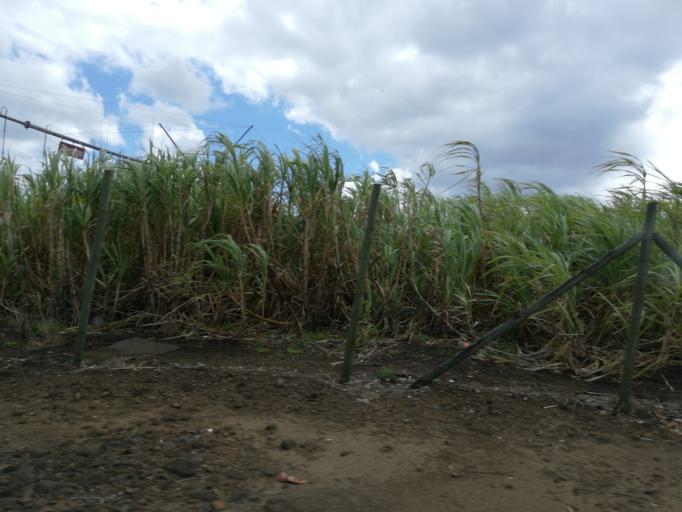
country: MU
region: Riviere du Rempart
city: Esperance Trebuchet
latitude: -20.0734
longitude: 57.6634
